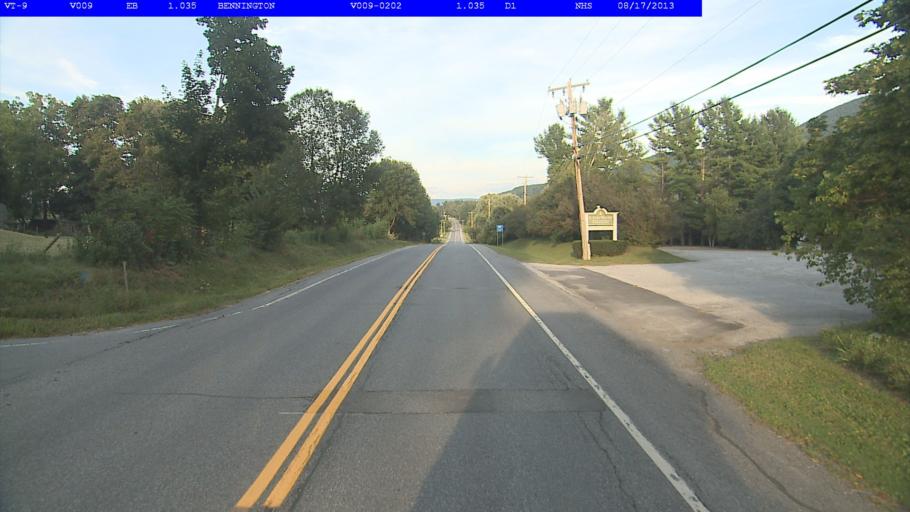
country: US
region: Vermont
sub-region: Bennington County
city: North Bennington
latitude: 42.8774
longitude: -73.2582
